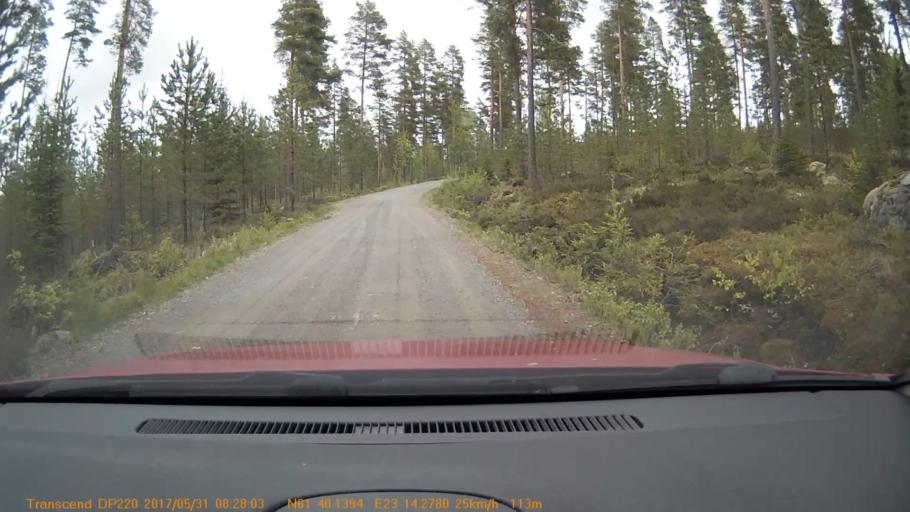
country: FI
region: Pirkanmaa
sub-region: Tampere
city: Viljakkala
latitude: 61.6690
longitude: 23.2380
